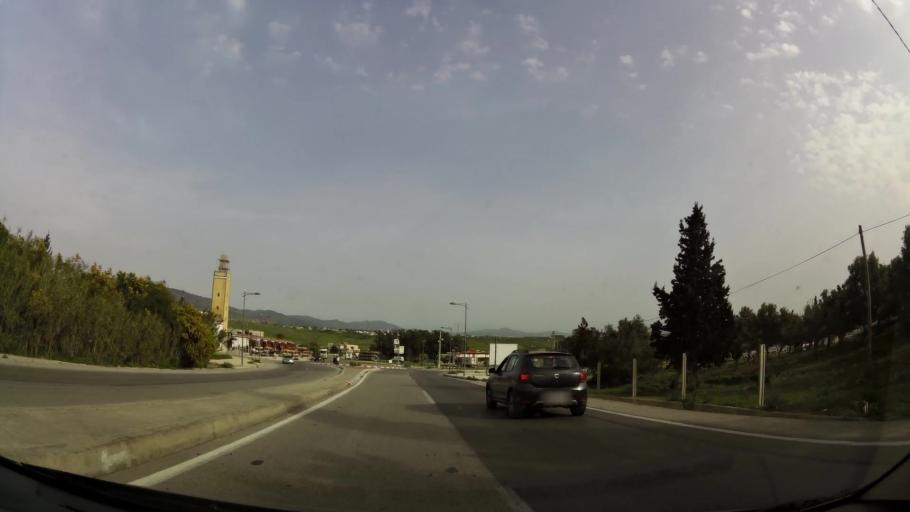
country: MA
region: Tanger-Tetouan
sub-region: Tanger-Assilah
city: Dar Chaoui
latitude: 35.6566
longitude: -5.6917
